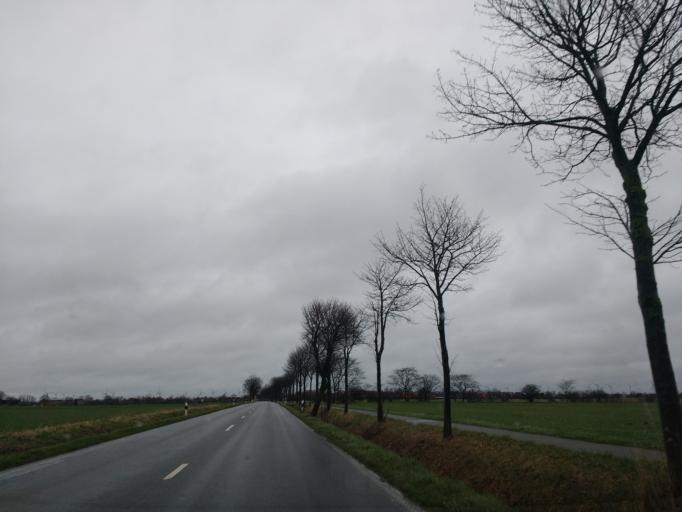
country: DE
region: Schleswig-Holstein
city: Fehmarn
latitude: 54.4502
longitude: 11.2037
